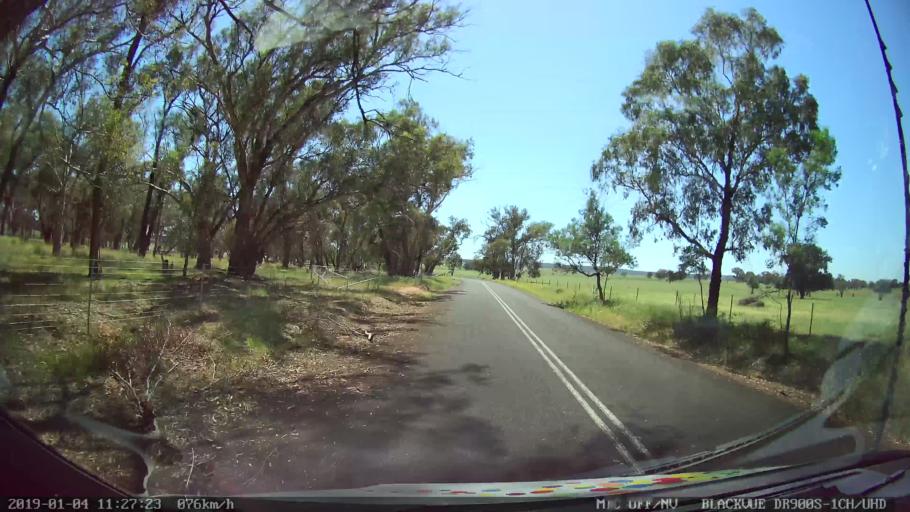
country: AU
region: New South Wales
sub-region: Cabonne
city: Molong
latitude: -33.1093
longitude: 148.7622
